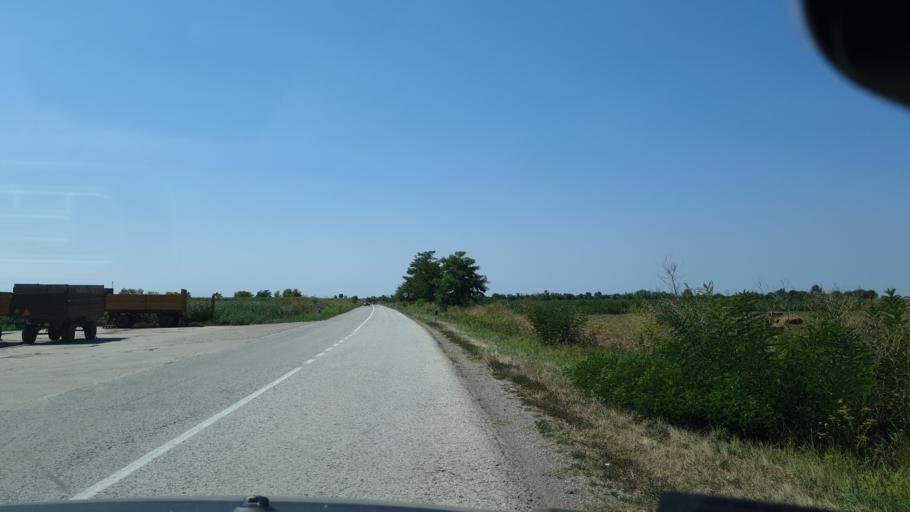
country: RS
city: Zmajevo
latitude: 45.4466
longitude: 19.7182
